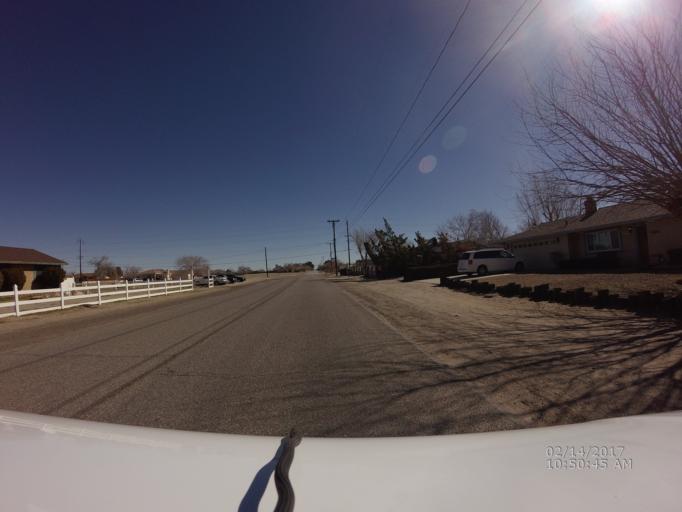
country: US
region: California
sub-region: Los Angeles County
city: Littlerock
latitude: 34.5689
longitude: -117.9350
